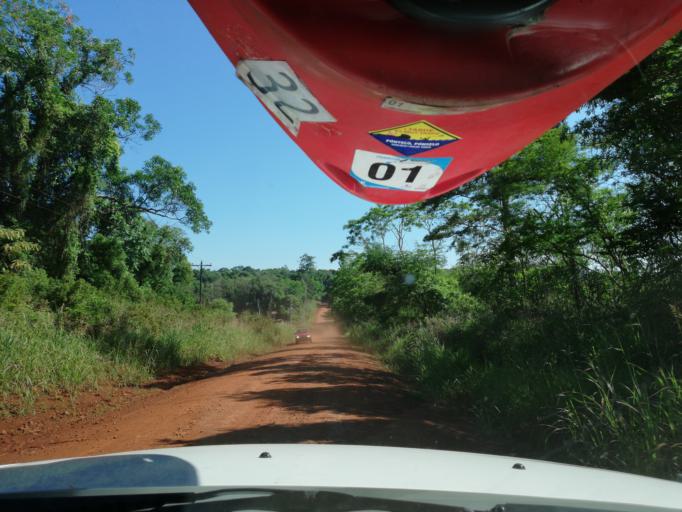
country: AR
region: Misiones
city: Puerto Leoni
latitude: -26.9719
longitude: -55.1646
